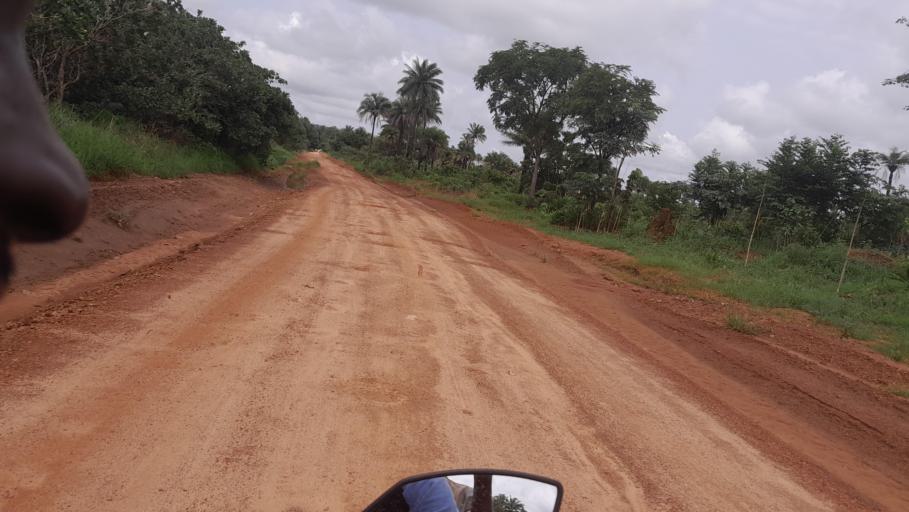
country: GN
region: Boke
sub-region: Boffa
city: Boffa
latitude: 10.0913
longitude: -13.8609
